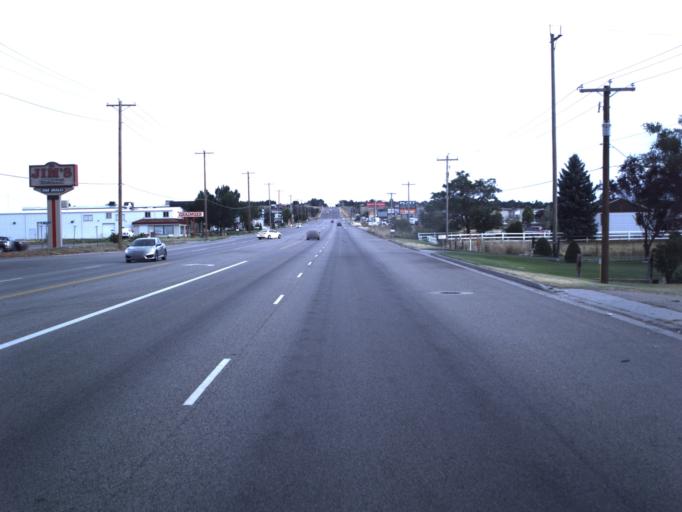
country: US
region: Utah
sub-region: Weber County
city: West Haven
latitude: 41.2131
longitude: -112.0259
